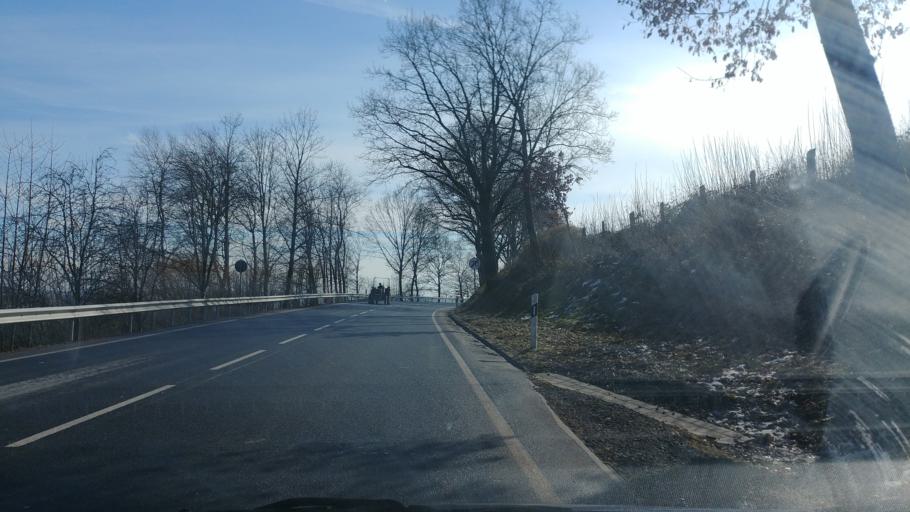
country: DE
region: Lower Saxony
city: Bodenfelde
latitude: 51.6834
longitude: 9.5686
